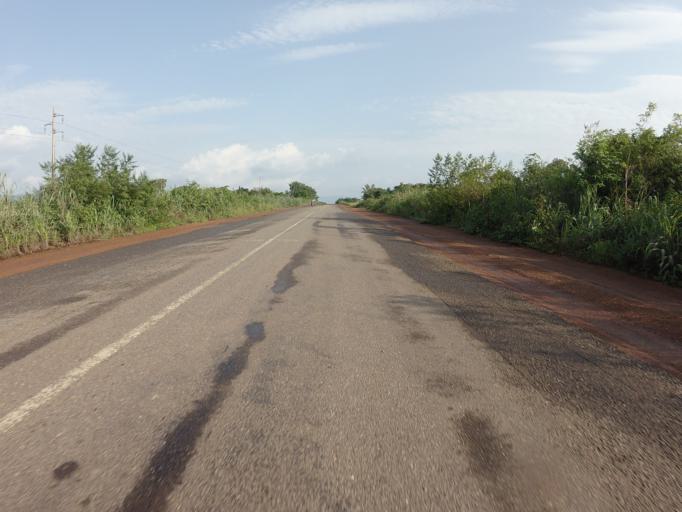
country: GH
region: Volta
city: Hohoe
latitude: 7.0275
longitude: 0.4276
